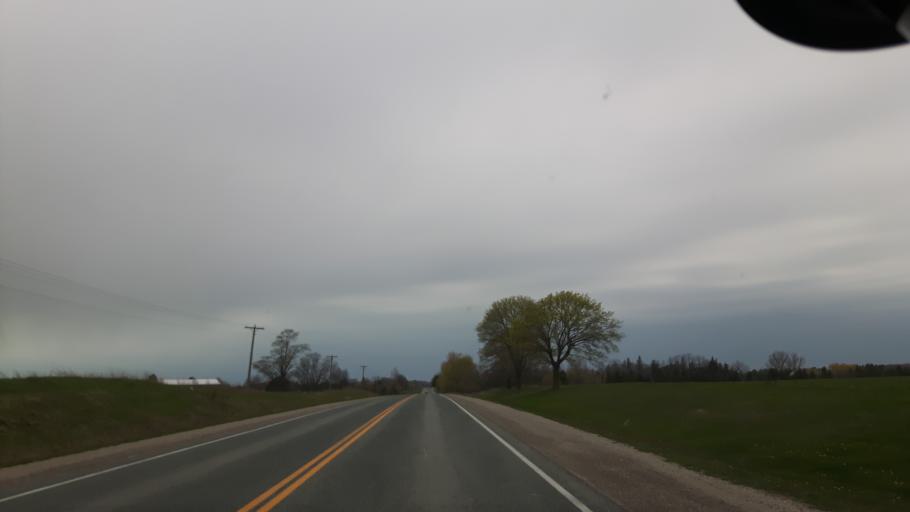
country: CA
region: Ontario
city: Bluewater
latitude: 43.6291
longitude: -81.5674
